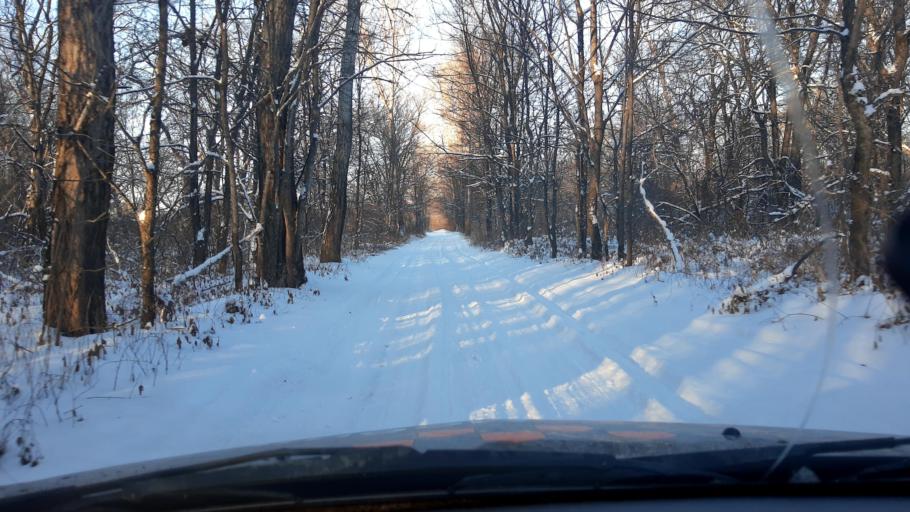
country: RU
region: Bashkortostan
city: Ufa
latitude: 54.6557
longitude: 55.9717
